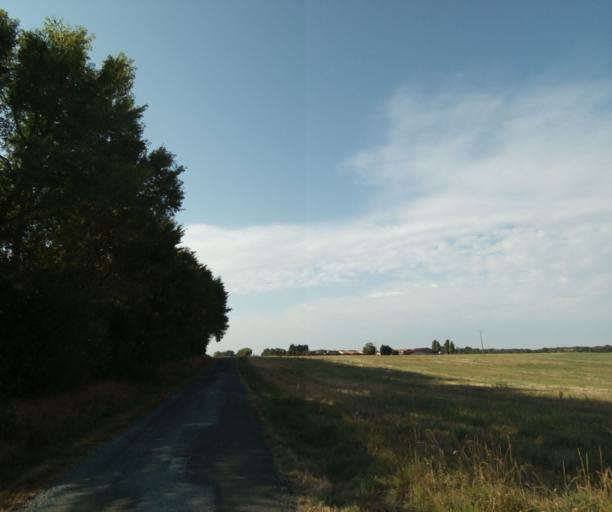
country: FR
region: Poitou-Charentes
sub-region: Departement de la Charente-Maritime
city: Cabariot
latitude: 45.9717
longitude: -0.8280
